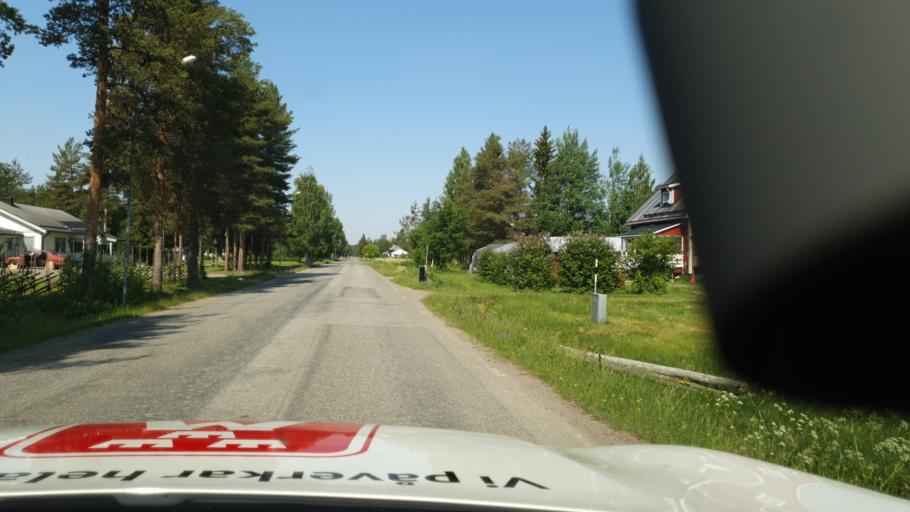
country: SE
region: Vaesterbotten
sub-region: Skelleftea Kommun
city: Langsele
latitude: 64.9478
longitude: 19.9341
